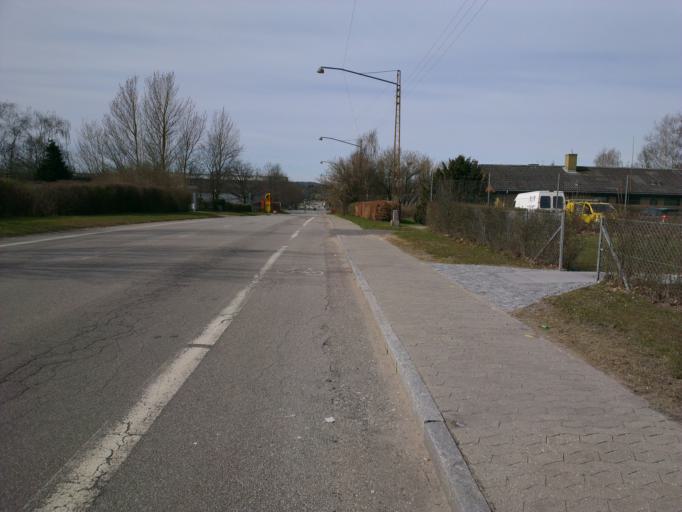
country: DK
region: Capital Region
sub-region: Frederikssund Kommune
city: Frederikssund
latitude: 55.8477
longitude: 12.0688
